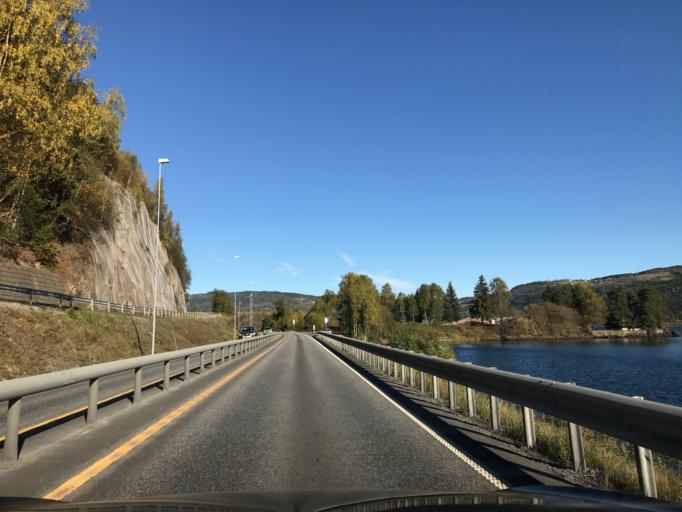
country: NO
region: Hedmark
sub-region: Ringsaker
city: Moelv
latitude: 60.9460
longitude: 10.6415
